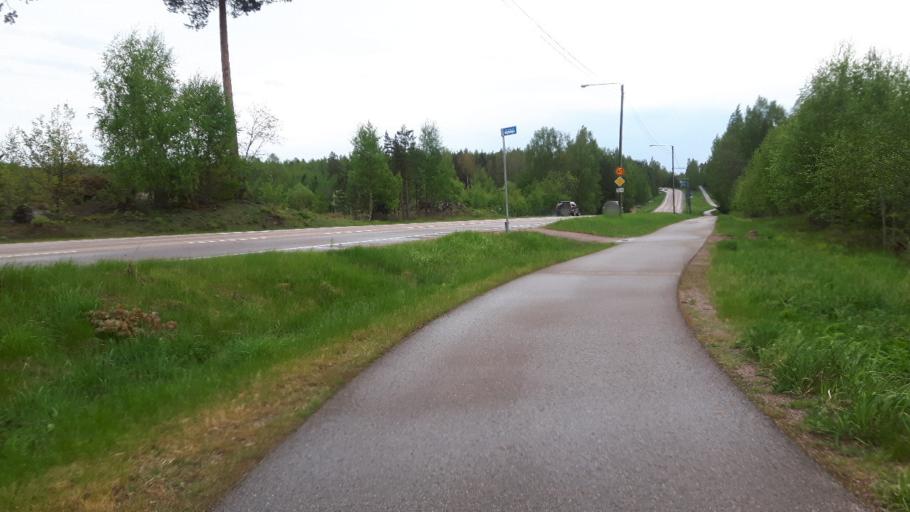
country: FI
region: Kymenlaakso
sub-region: Kotka-Hamina
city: Hamina
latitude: 60.5656
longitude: 27.1058
